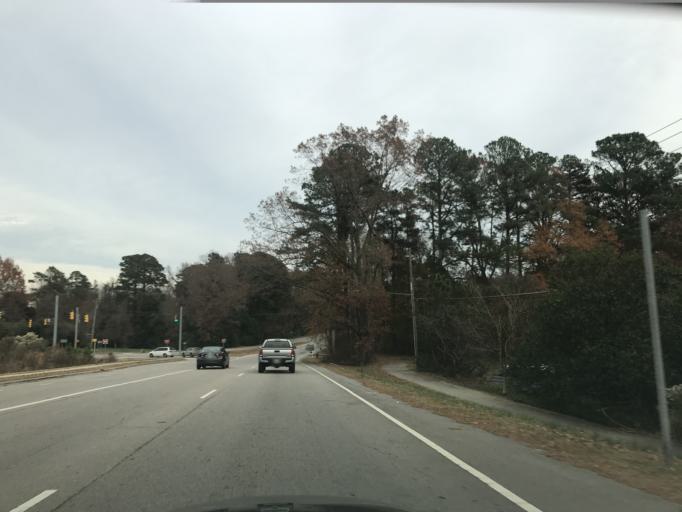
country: US
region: North Carolina
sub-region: Wake County
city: West Raleigh
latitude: 35.7858
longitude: -78.7189
